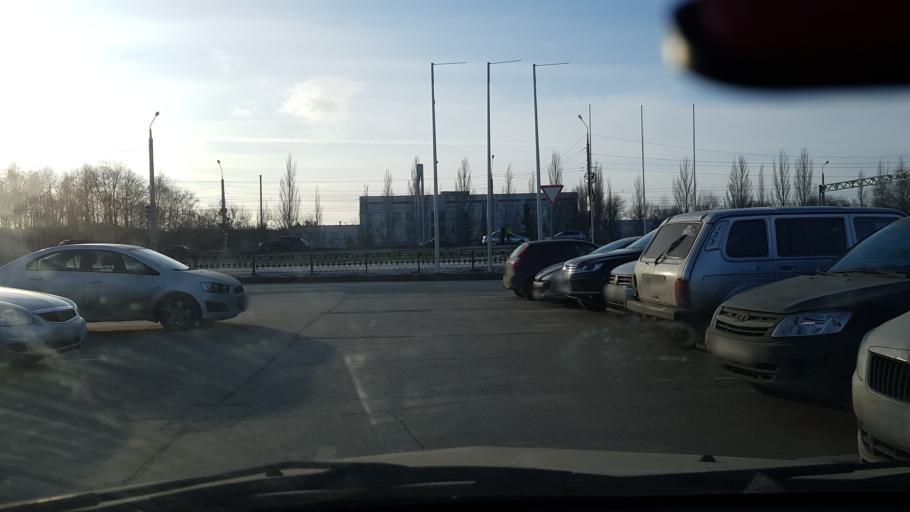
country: RU
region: Samara
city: Tol'yatti
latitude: 53.5413
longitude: 49.3878
